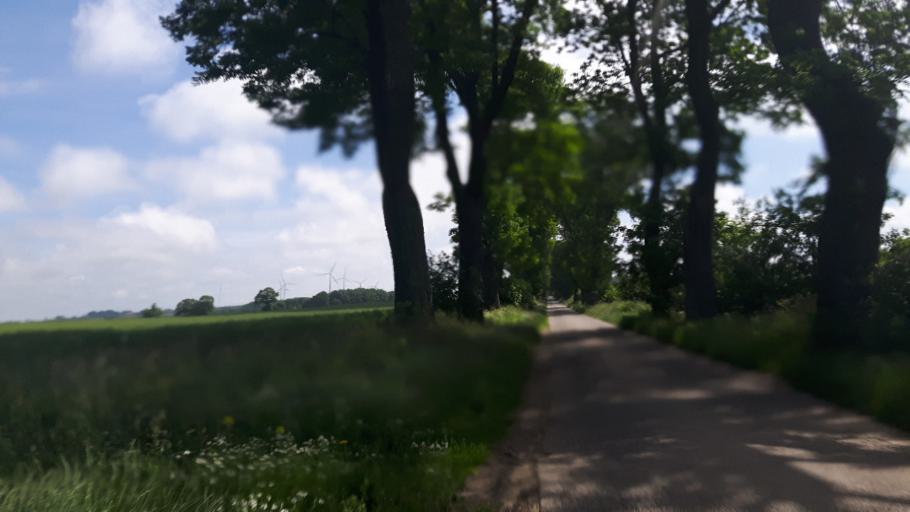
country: PL
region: West Pomeranian Voivodeship
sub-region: Powiat slawienski
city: Darlowo
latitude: 54.4704
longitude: 16.4758
